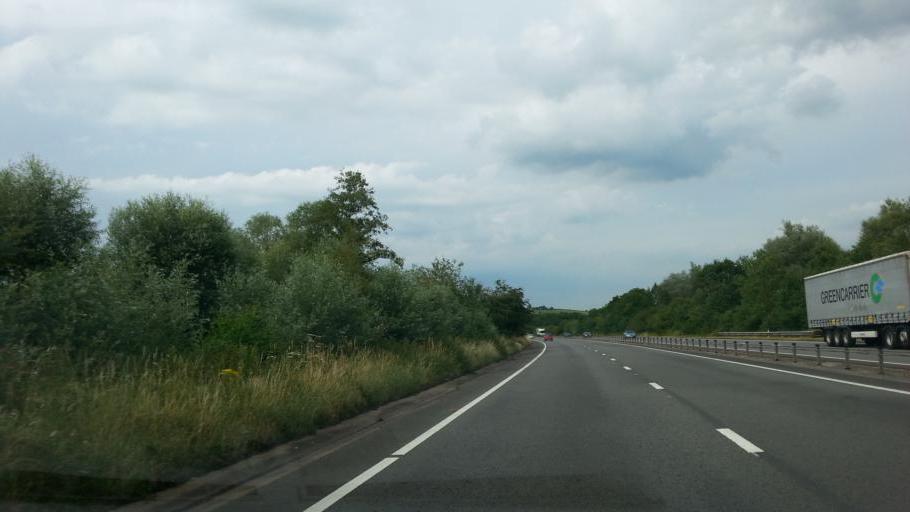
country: GB
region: Wales
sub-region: Monmouthshire
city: Llangwm
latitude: 51.7278
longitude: -2.8477
